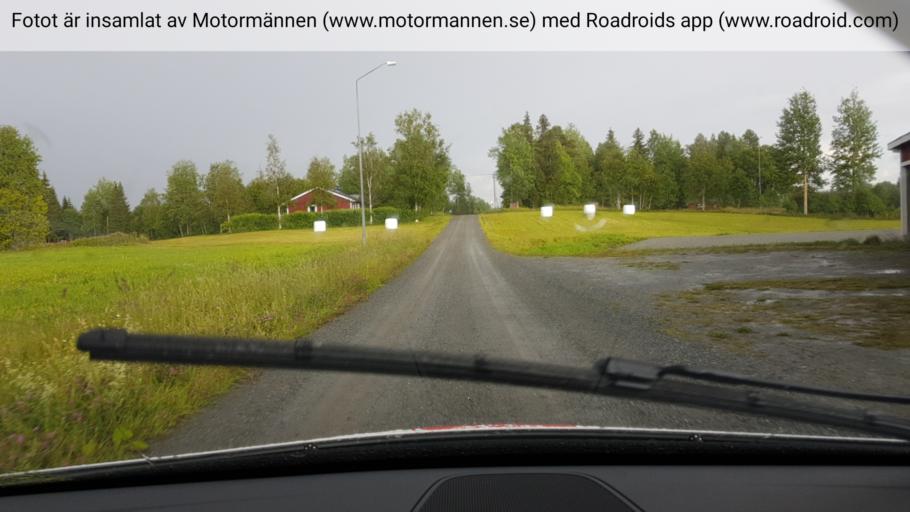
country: SE
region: Jaemtland
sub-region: OEstersunds Kommun
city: Ostersund
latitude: 63.0505
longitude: 14.6792
